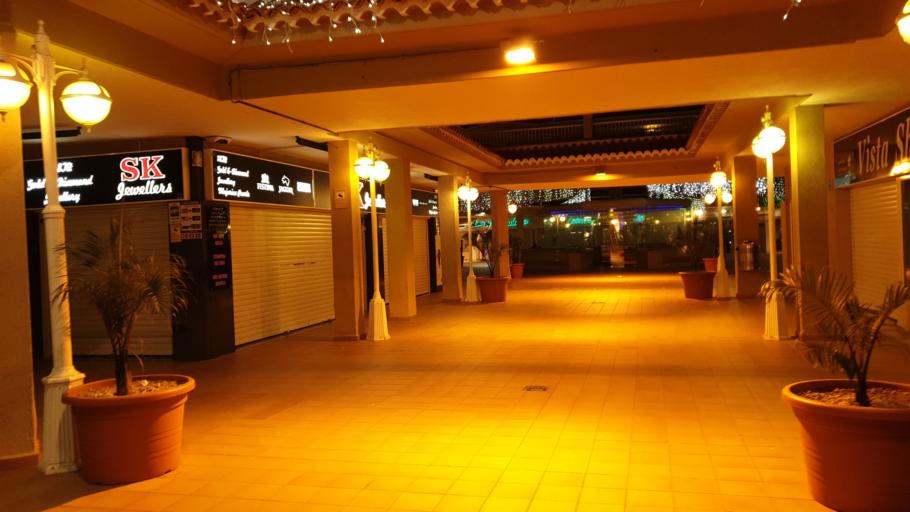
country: ES
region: Canary Islands
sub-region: Provincia de Santa Cruz de Tenerife
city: Playa de las Americas
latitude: 28.0538
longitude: -16.7270
